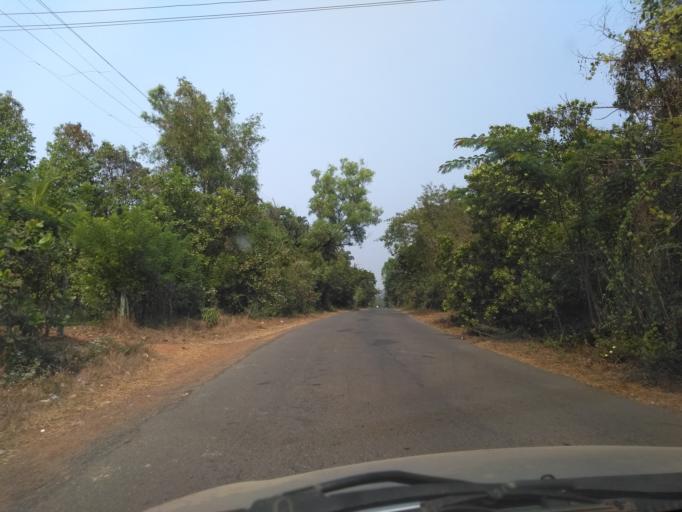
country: IN
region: Goa
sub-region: North Goa
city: Dicholi
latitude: 15.7164
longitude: 73.9545
